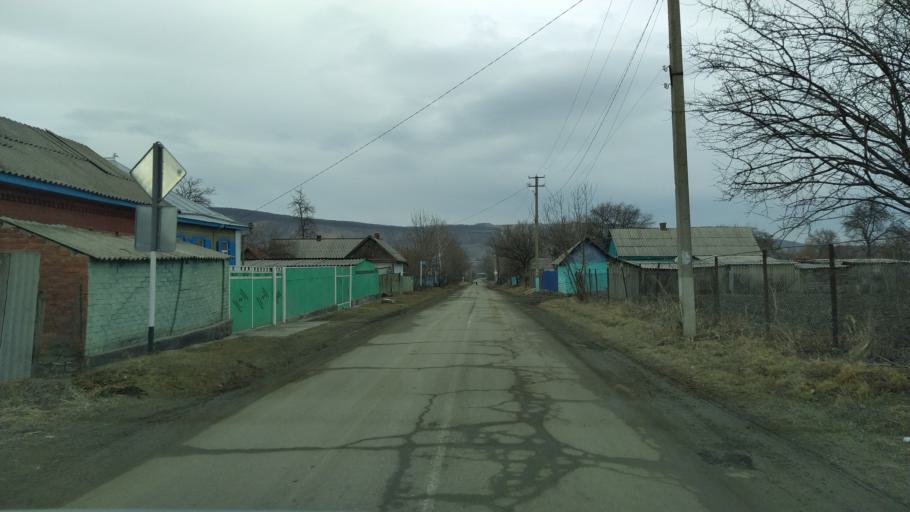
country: RU
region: Krasnodarskiy
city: Peredovaya
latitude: 44.1196
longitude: 41.4750
